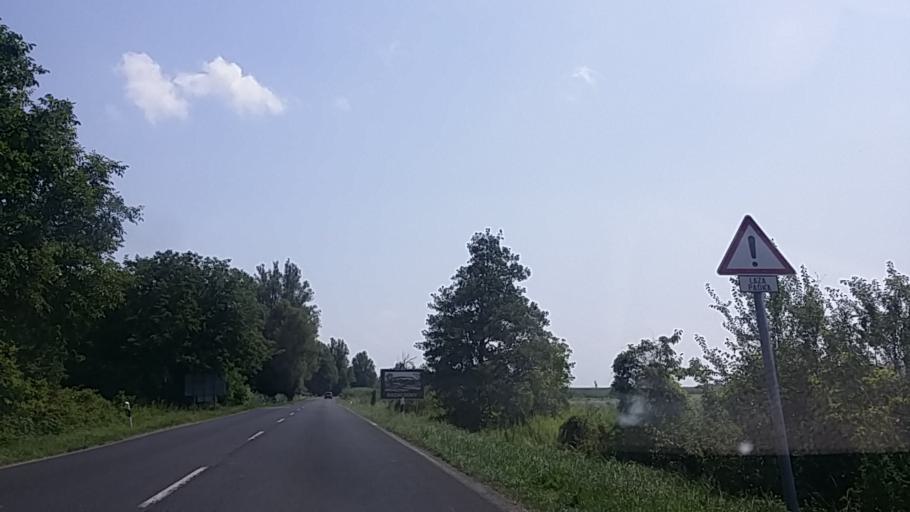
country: HU
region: Veszprem
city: Badacsonytomaj
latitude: 46.8060
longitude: 17.4674
